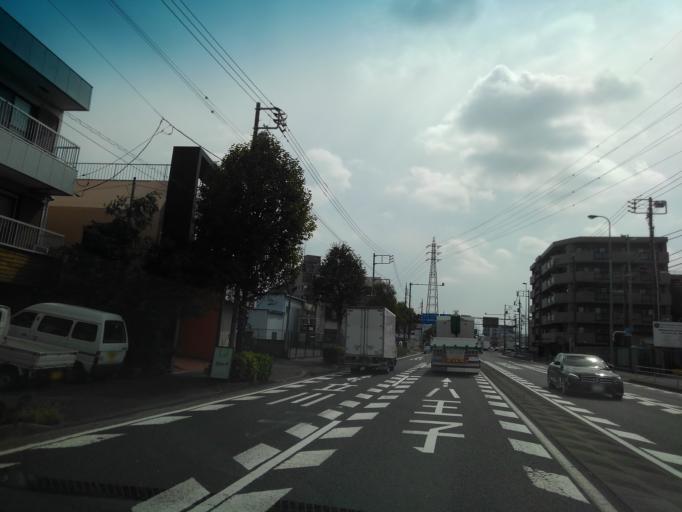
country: JP
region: Tokyo
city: Fussa
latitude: 35.7267
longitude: 139.3431
